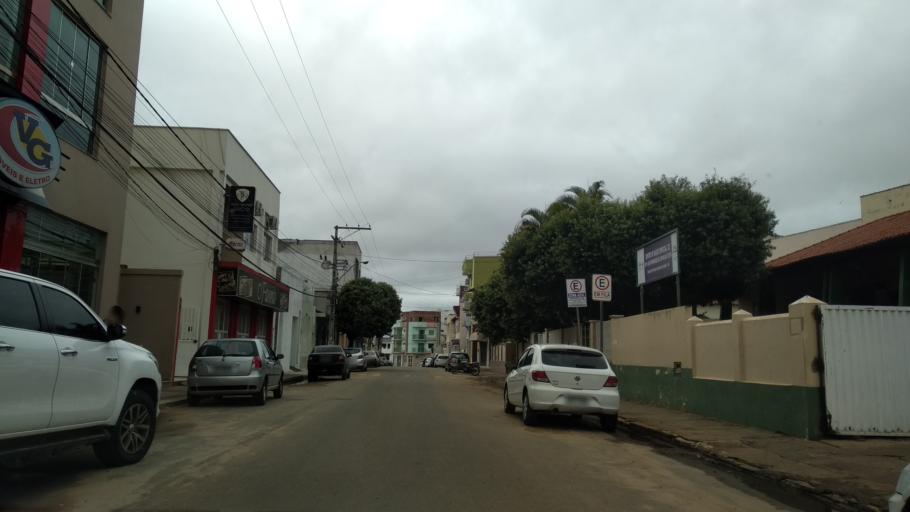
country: BR
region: Bahia
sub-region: Caetite
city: Caetite
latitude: -14.0680
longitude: -42.4888
